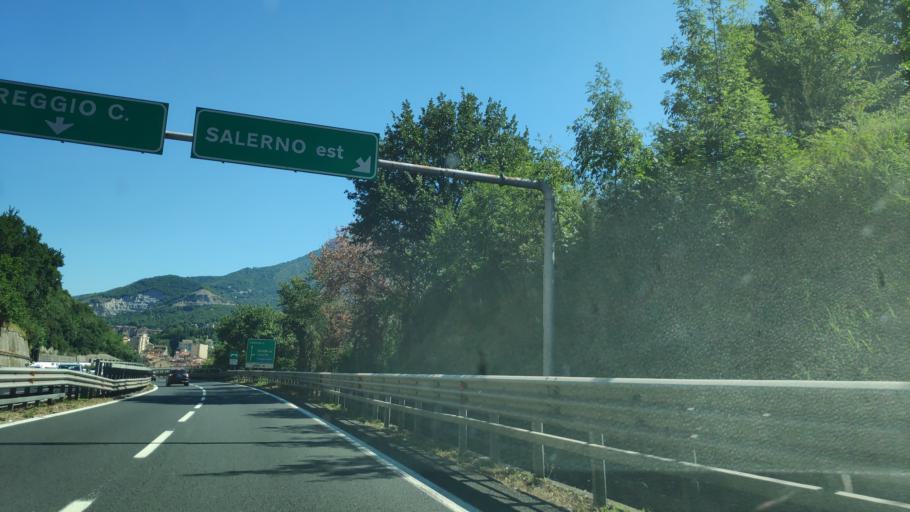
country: IT
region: Campania
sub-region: Provincia di Salerno
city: Capezzano Inferiore
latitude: 40.6888
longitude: 14.7732
